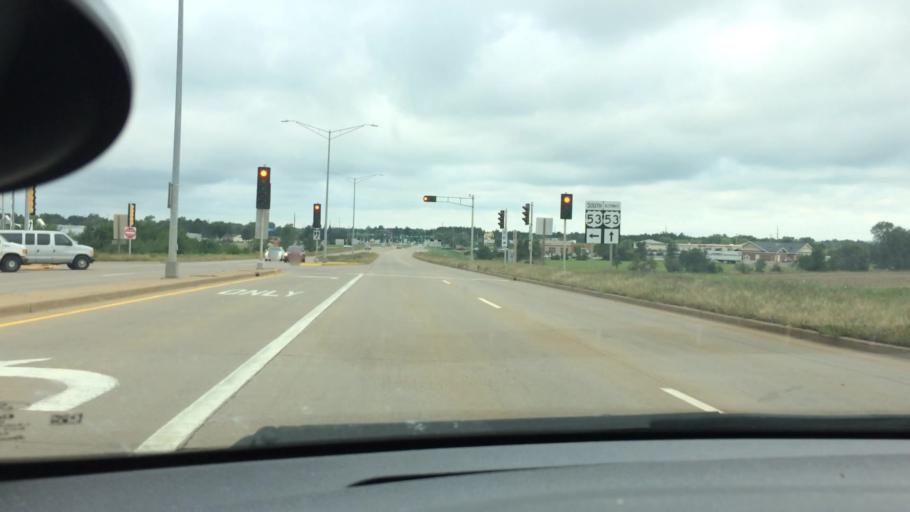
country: US
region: Wisconsin
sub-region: Chippewa County
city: Lake Hallie
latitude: 44.8831
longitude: -91.4151
